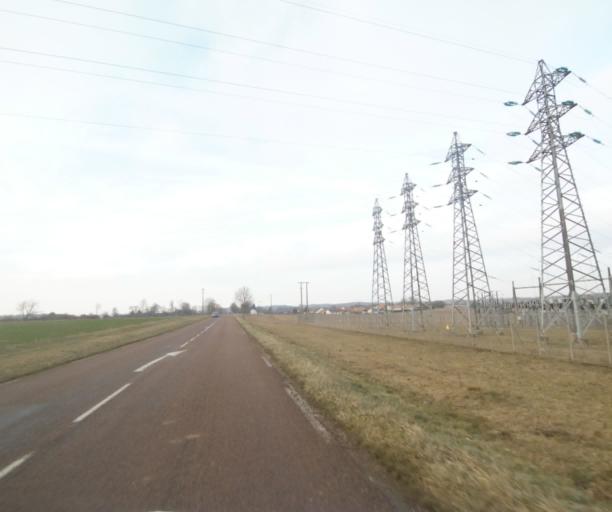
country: FR
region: Champagne-Ardenne
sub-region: Departement de la Haute-Marne
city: Chancenay
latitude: 48.6762
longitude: 4.9983
